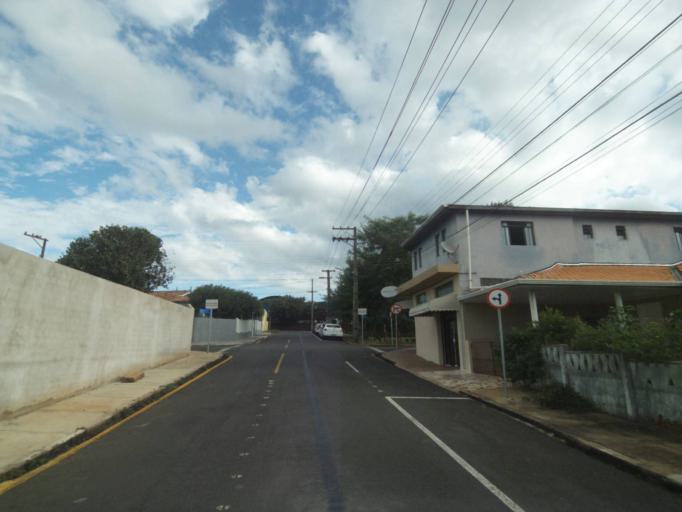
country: BR
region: Parana
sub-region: Telemaco Borba
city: Telemaco Borba
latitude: -24.3381
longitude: -50.6119
